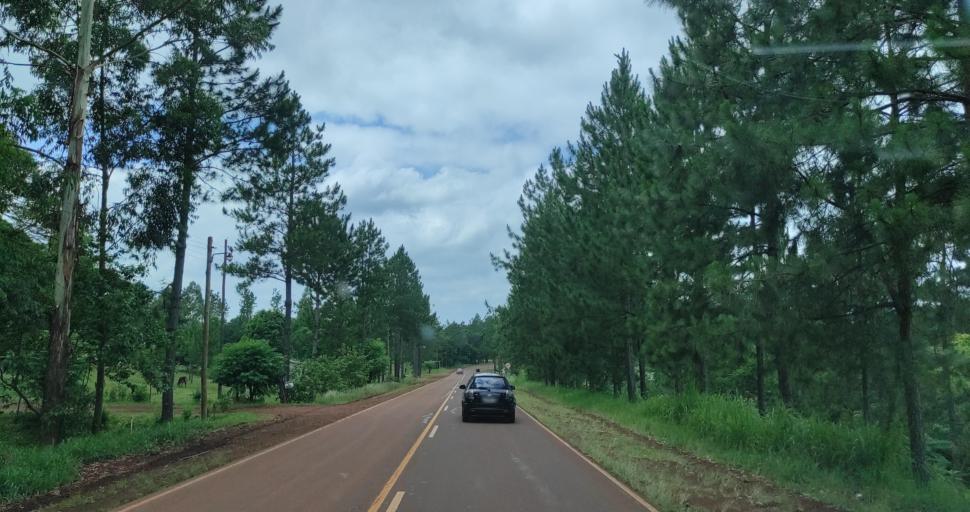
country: AR
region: Misiones
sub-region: Departamento de Veinticinco de Mayo
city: Veinticinco de Mayo
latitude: -27.4170
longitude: -54.7360
